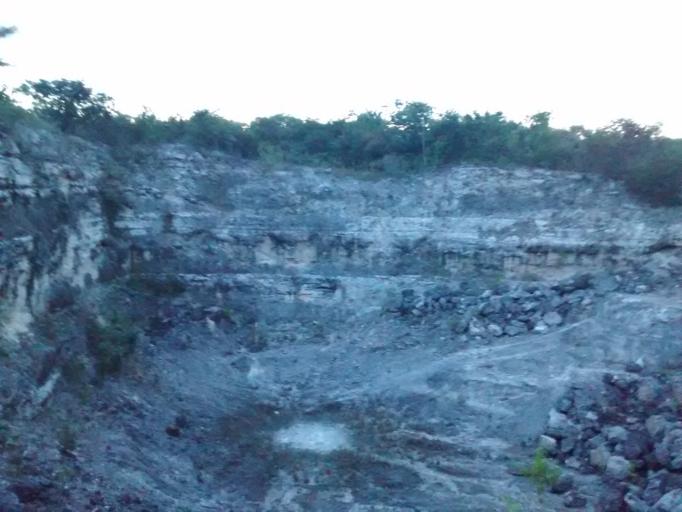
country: MX
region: Yucatan
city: Chichimila
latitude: 20.4660
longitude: -88.2255
